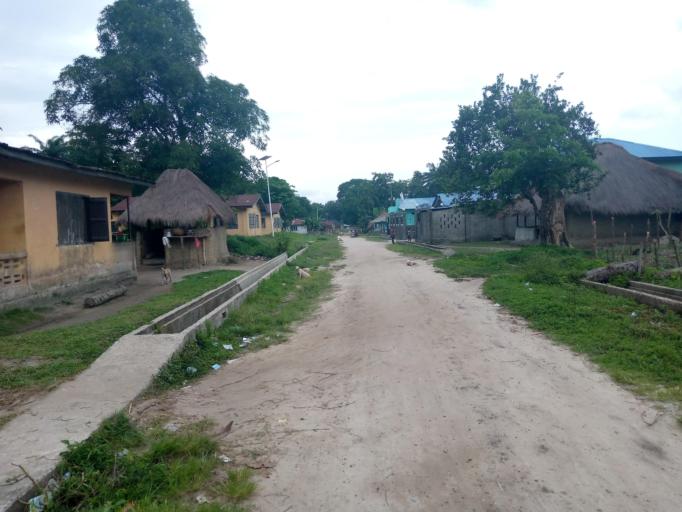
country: SL
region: Southern Province
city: Bonthe
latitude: 7.5297
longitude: -12.5072
